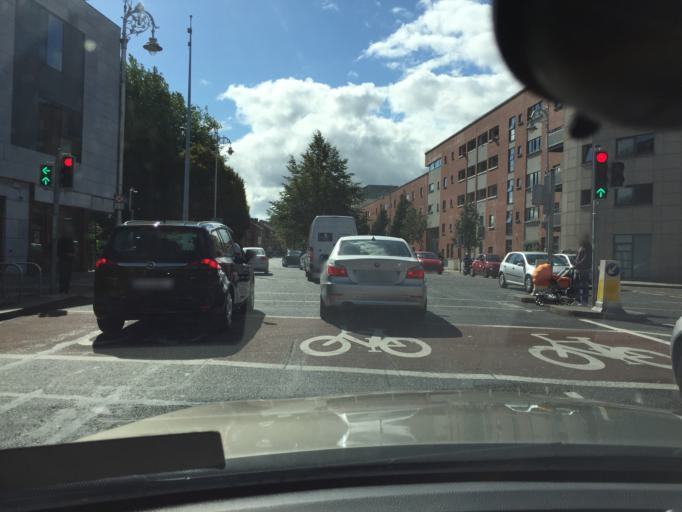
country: IE
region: Leinster
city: Rathmines
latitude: 53.3391
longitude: -6.2726
